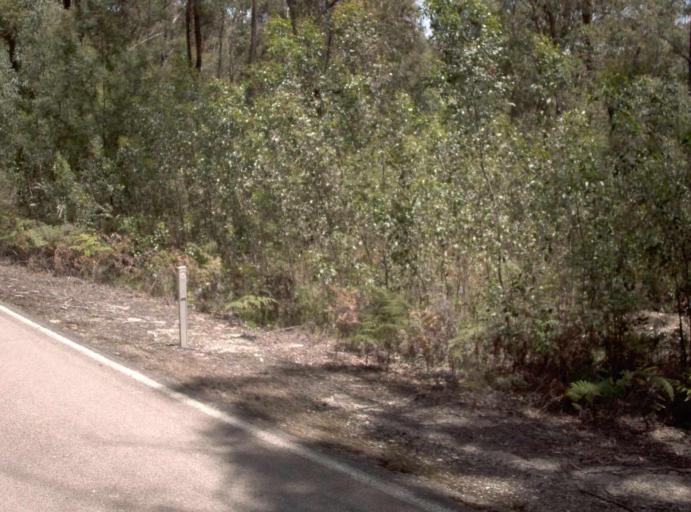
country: AU
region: Victoria
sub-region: East Gippsland
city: Lakes Entrance
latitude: -37.6489
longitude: 147.8930
